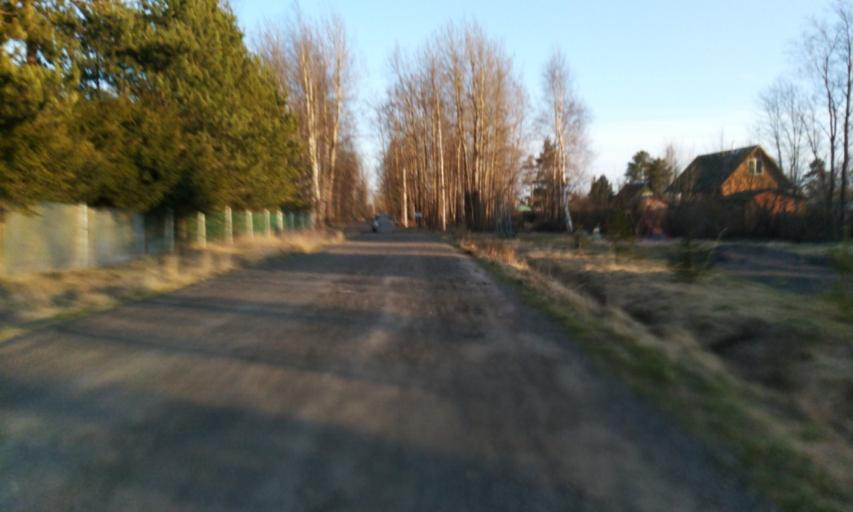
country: RU
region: Leningrad
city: Novoye Devyatkino
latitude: 60.0877
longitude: 30.4572
